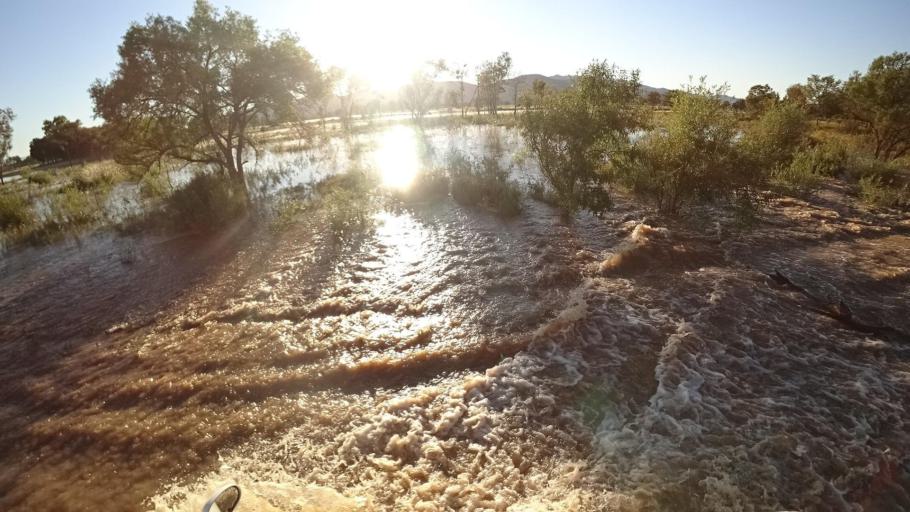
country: RU
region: Primorskiy
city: Kirovskiy
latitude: 44.7778
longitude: 133.6263
